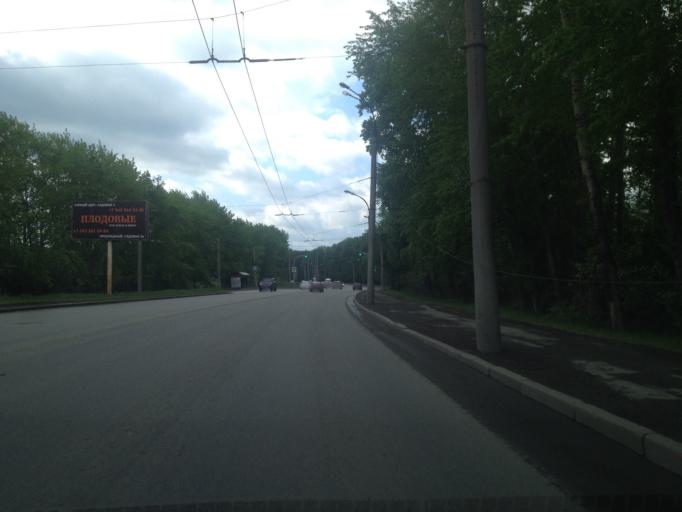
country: RU
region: Sverdlovsk
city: Yekaterinburg
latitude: 56.7630
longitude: 60.6720
